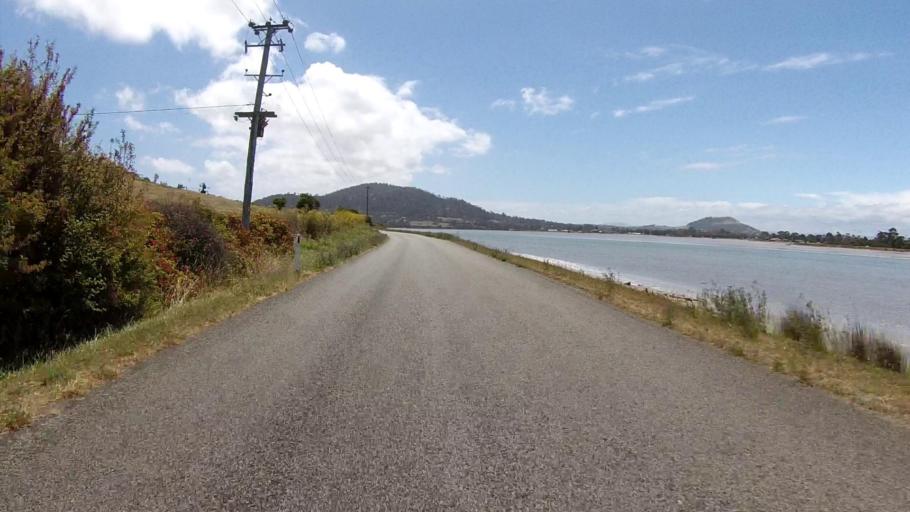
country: AU
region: Tasmania
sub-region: Clarence
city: Lauderdale
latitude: -42.9237
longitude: 147.4812
